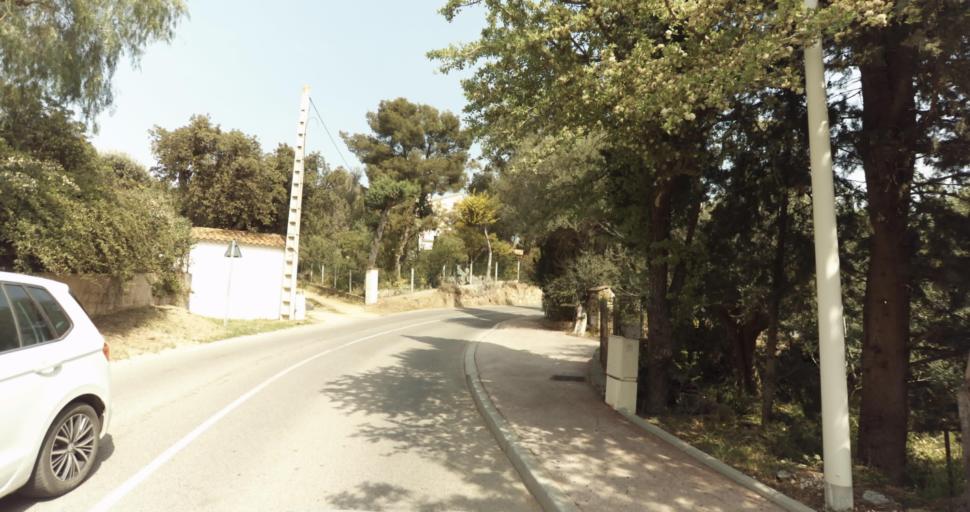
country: FR
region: Provence-Alpes-Cote d'Azur
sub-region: Departement du Var
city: Bormes-les-Mimosas
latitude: 43.1447
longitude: 6.3485
